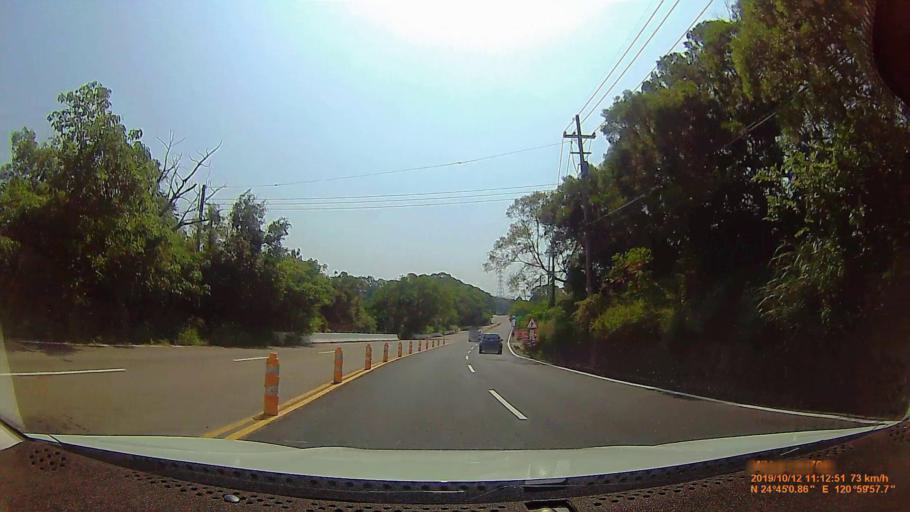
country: TW
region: Taiwan
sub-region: Hsinchu
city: Hsinchu
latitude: 24.7501
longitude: 120.9992
